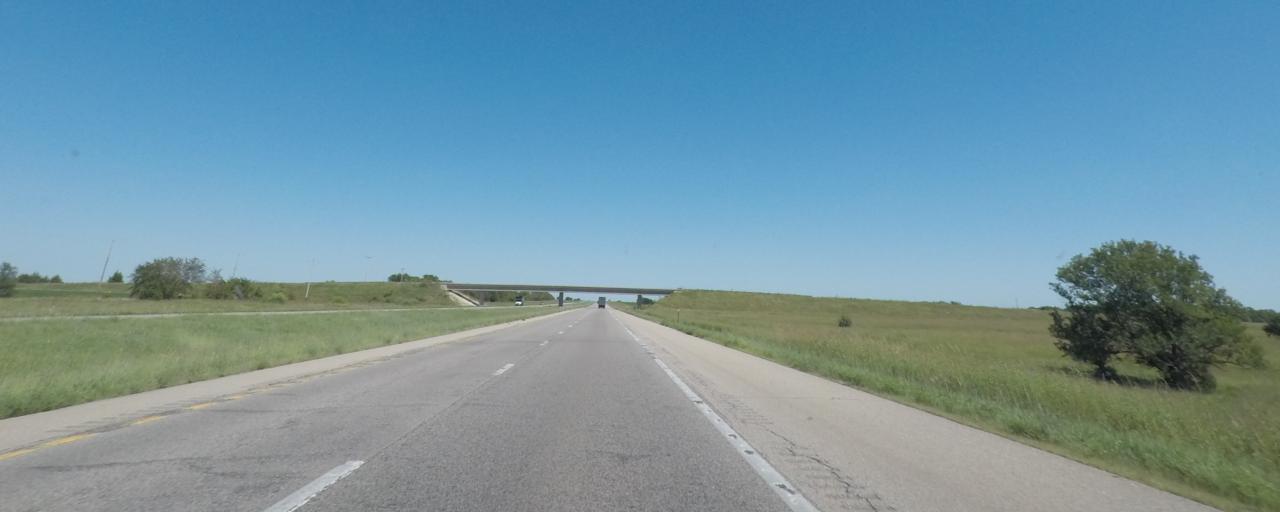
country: US
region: Kansas
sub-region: Osage County
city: Osage City
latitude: 38.4256
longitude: -95.8239
